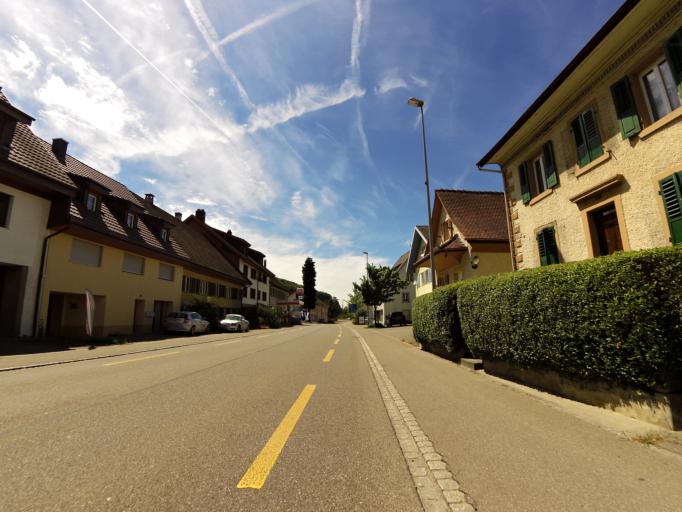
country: CH
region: Aargau
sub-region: Bezirk Rheinfelden
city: Stein
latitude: 47.5427
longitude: 7.9496
